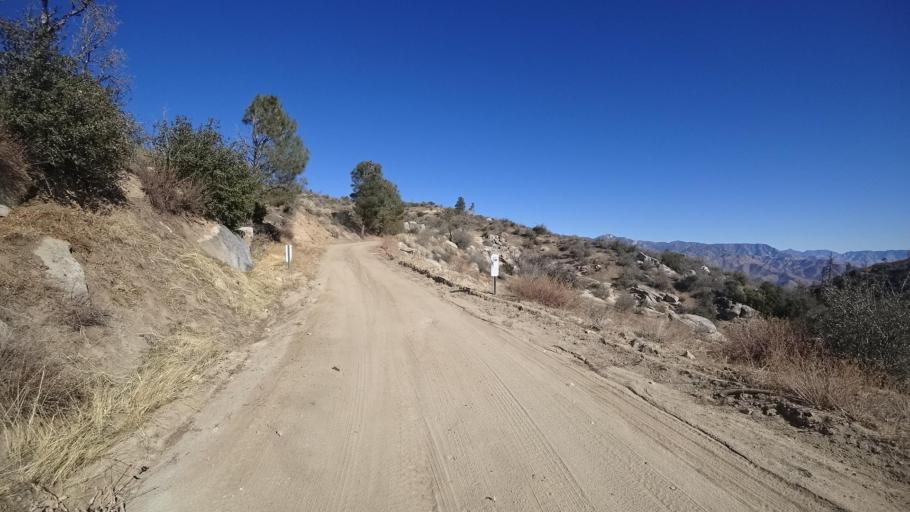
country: US
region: California
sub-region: Kern County
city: Alta Sierra
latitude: 35.7107
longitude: -118.5162
